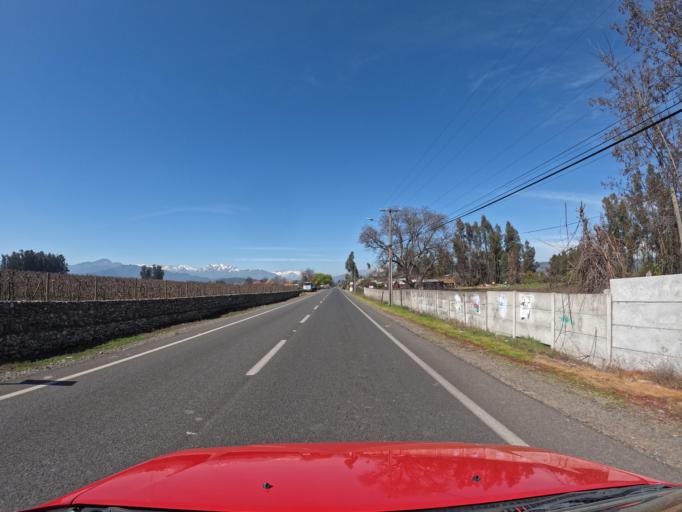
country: CL
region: Maule
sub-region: Provincia de Curico
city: Teno
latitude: -34.9663
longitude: -71.0358
